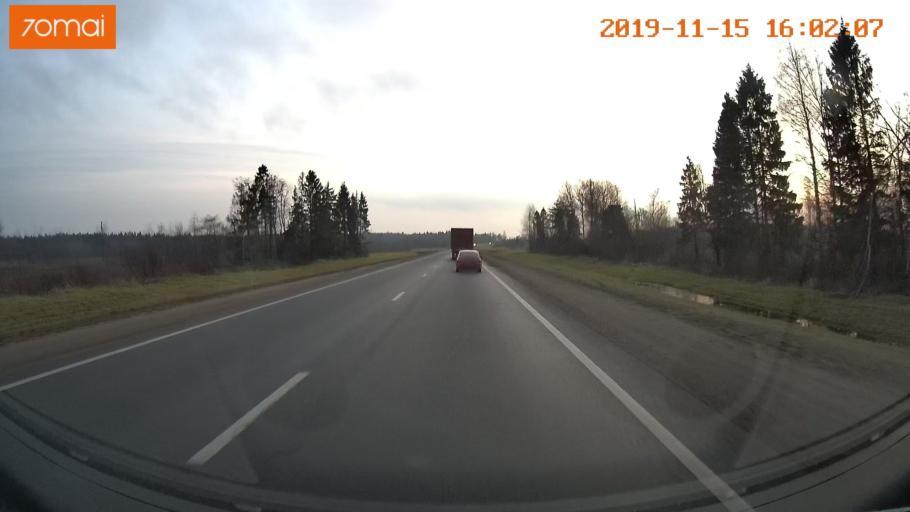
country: RU
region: Jaroslavl
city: Yaroslavl
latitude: 57.7749
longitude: 39.9267
